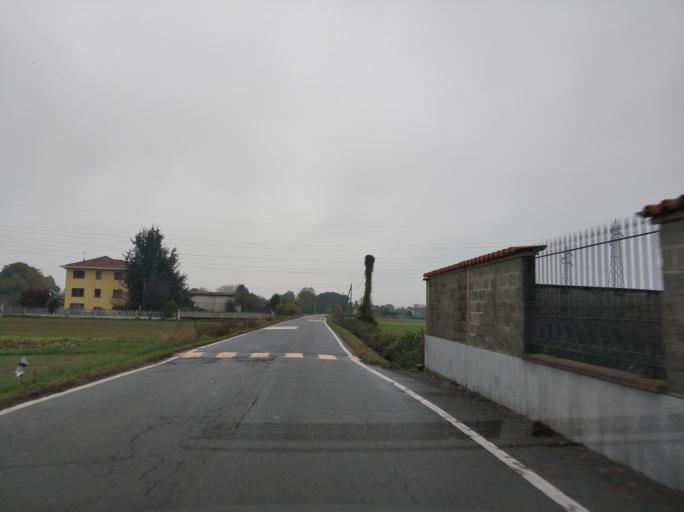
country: IT
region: Piedmont
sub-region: Provincia di Torino
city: Nole
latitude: 45.2350
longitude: 7.5713
